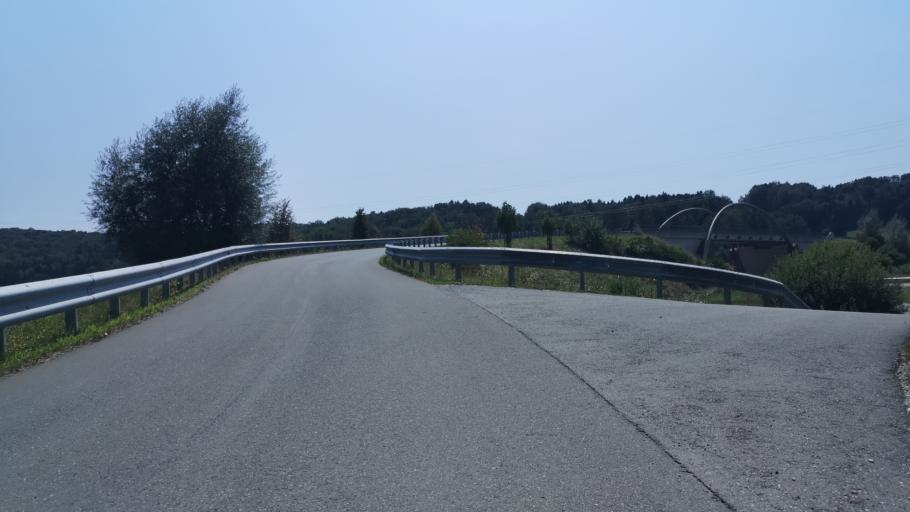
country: AT
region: Styria
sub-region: Politischer Bezirk Deutschlandsberg
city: Gross Sankt Florian
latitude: 46.8162
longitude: 15.2878
